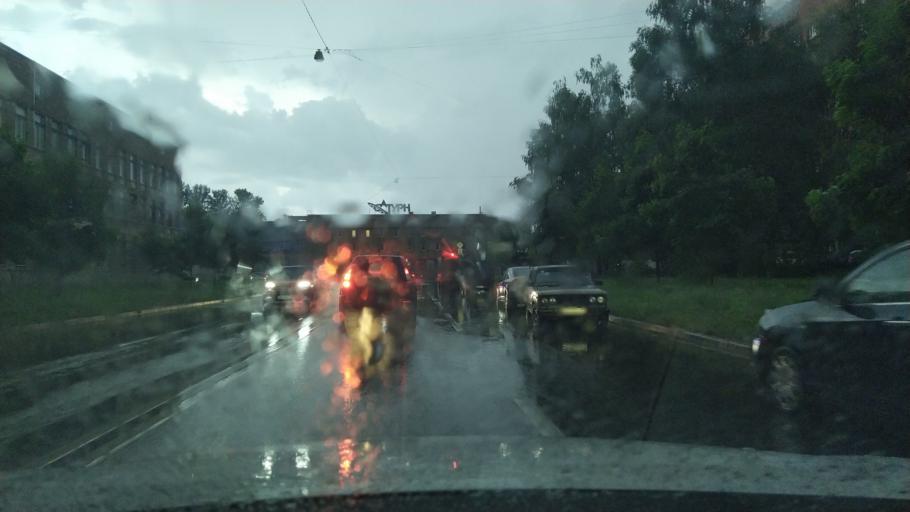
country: RU
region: Leningrad
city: Sampsonievskiy
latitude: 59.9797
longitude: 30.3545
